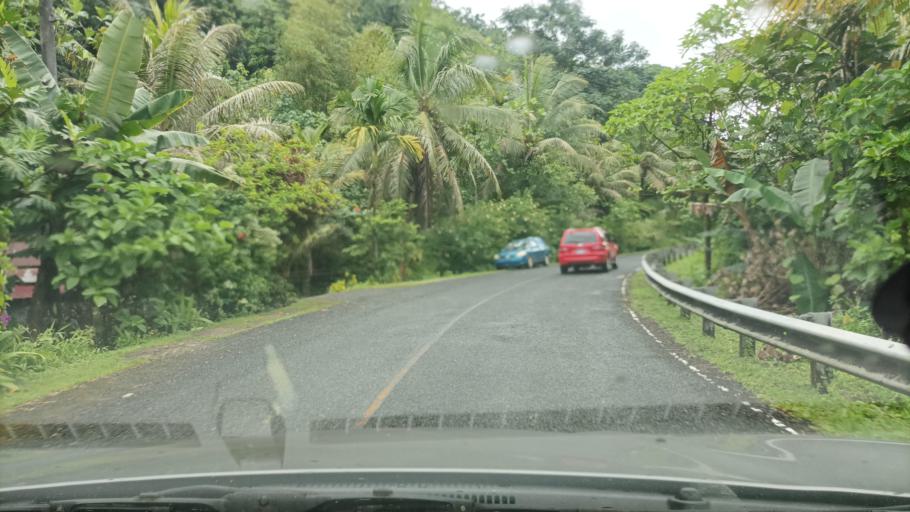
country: FM
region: Pohnpei
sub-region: Madolenihm Municipality
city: Madolenihm Municipality Government
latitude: 6.8070
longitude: 158.2667
